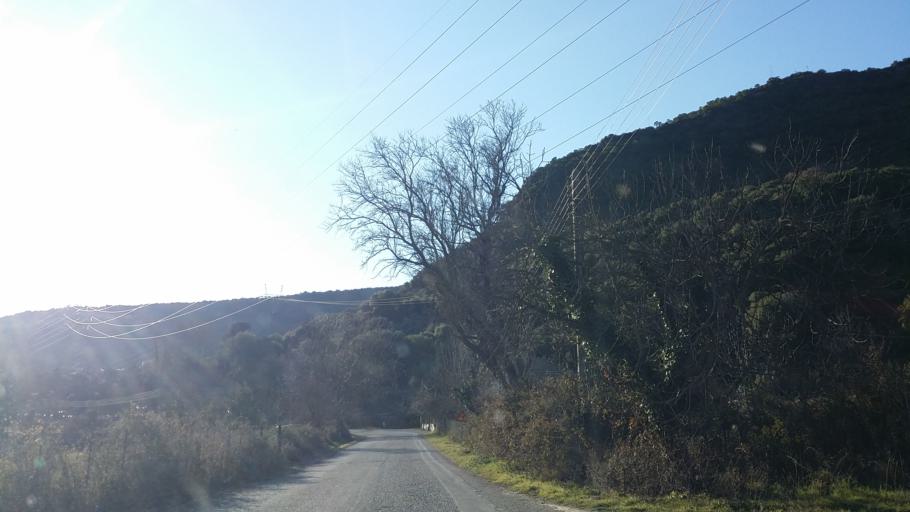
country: GR
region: West Greece
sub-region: Nomos Aitolias kai Akarnanias
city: Neapolis
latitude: 38.7675
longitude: 21.4396
